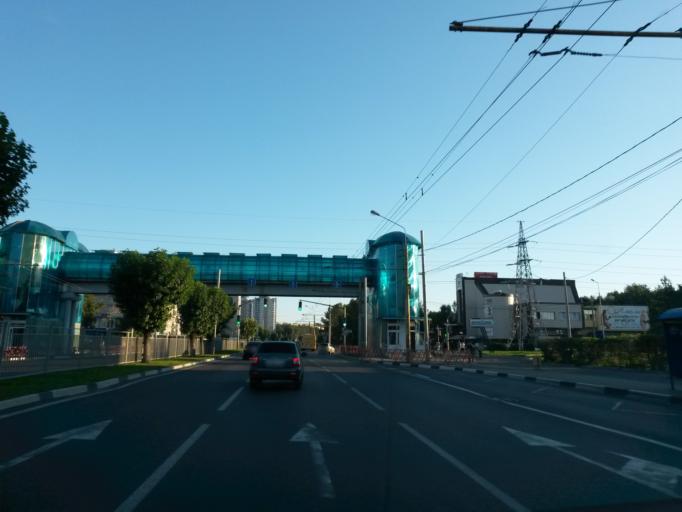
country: RU
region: Jaroslavl
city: Yaroslavl
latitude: 57.5862
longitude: 39.8565
